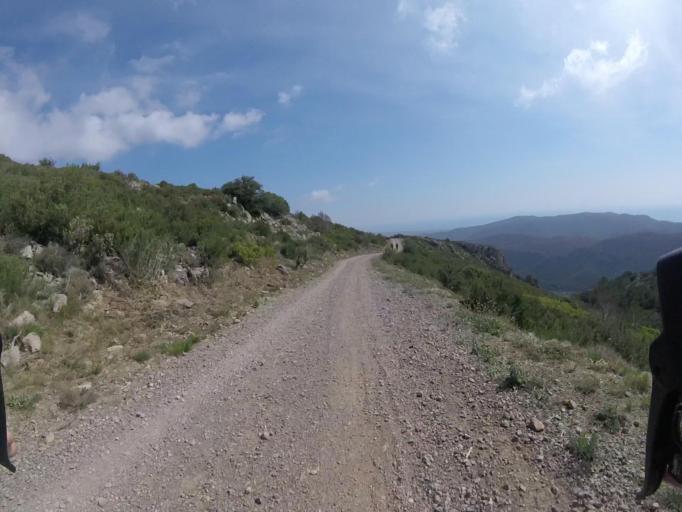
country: ES
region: Valencia
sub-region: Provincia de Castello
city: Benicassim
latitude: 40.0953
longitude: 0.0463
